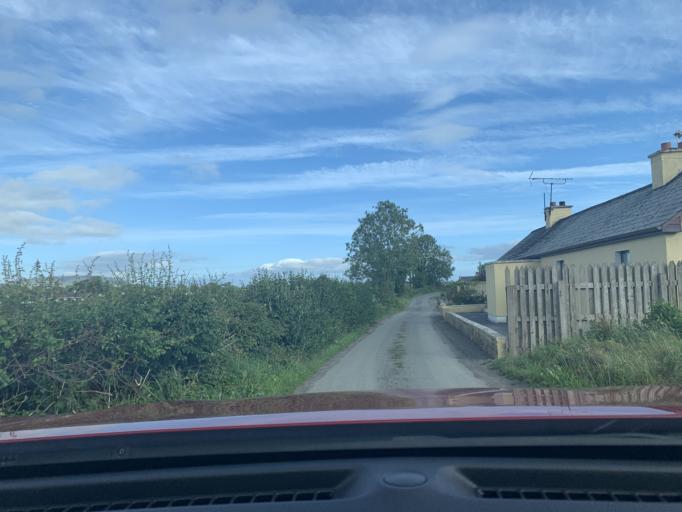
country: IE
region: Connaught
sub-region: Sligo
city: Sligo
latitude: 54.2355
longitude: -8.4689
